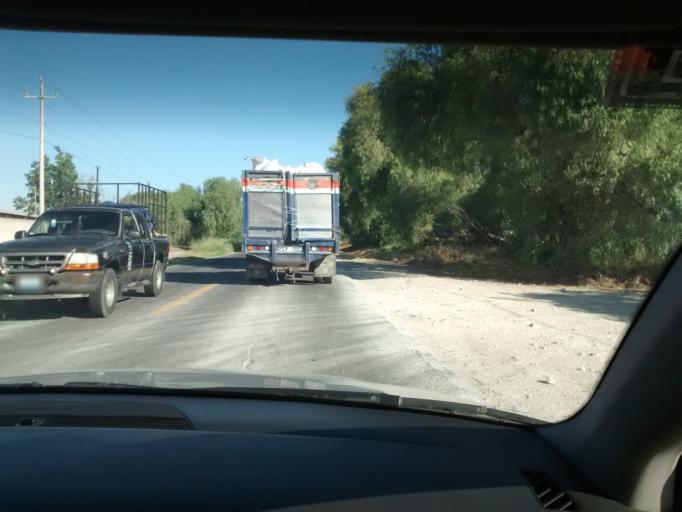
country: MX
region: Puebla
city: San Bartolo Teontepec
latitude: 18.5330
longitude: -97.5253
